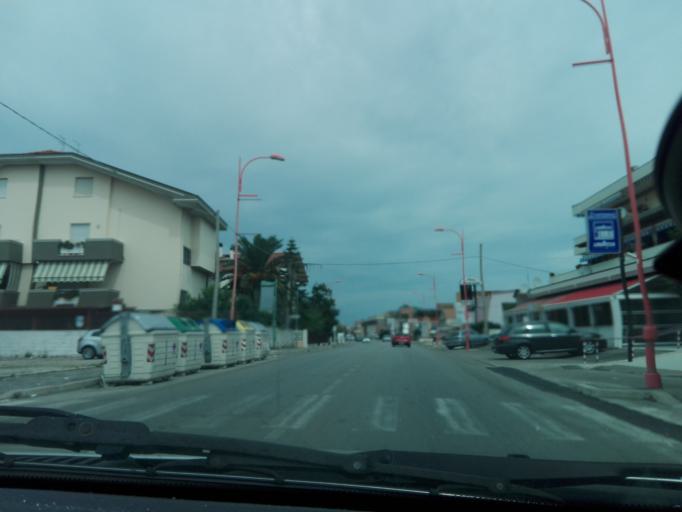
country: IT
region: Abruzzo
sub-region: Provincia di Pescara
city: Montesilvano Marina
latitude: 42.4986
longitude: 14.1682
